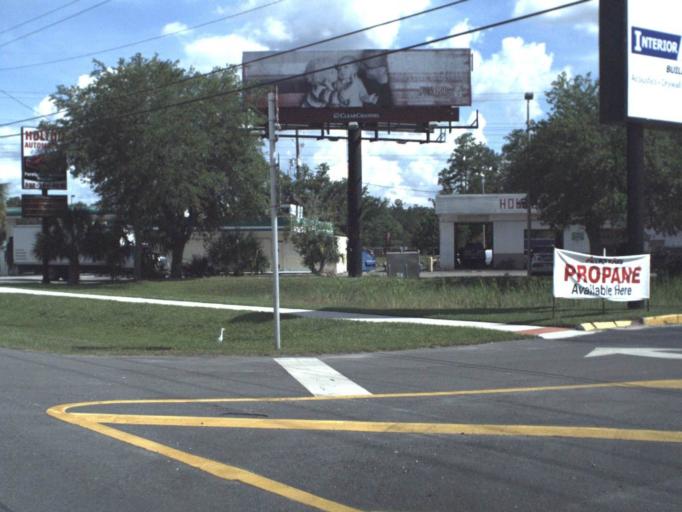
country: US
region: Florida
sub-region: Alachua County
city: Gainesville
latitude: 29.7045
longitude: -82.3453
